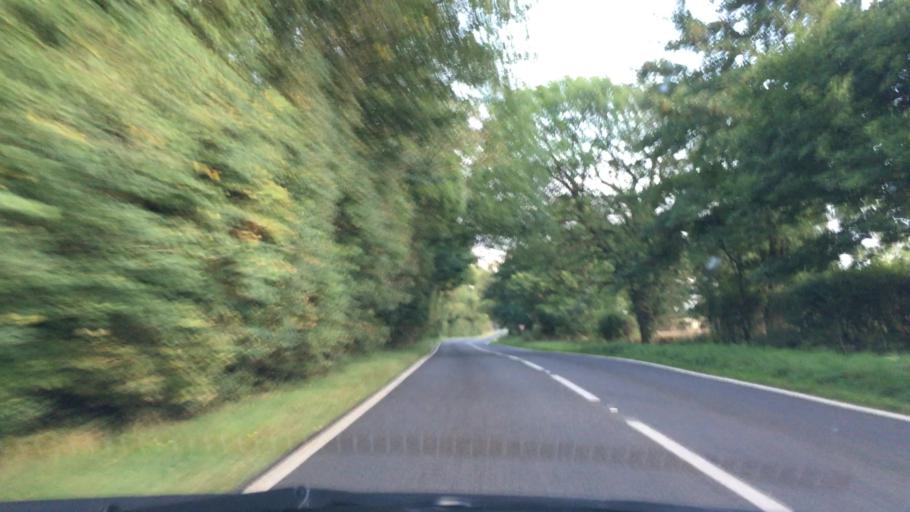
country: GB
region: England
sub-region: North East Lincolnshire
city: Wold Newton
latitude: 53.4742
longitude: -0.1136
